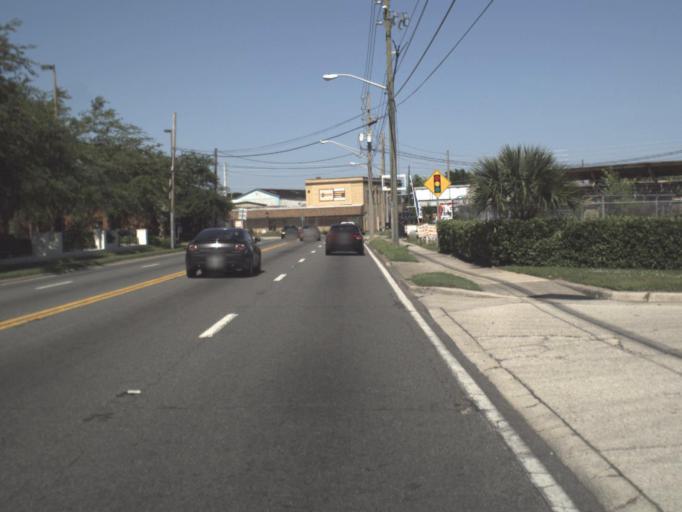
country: US
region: Florida
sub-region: Duval County
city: Jacksonville
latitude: 30.3363
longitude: -81.6781
